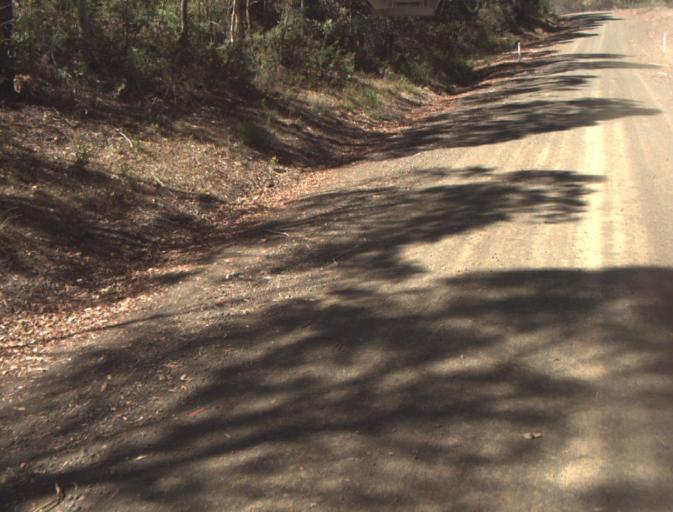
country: AU
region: Tasmania
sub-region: Launceston
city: Newstead
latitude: -41.3061
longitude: 147.3344
